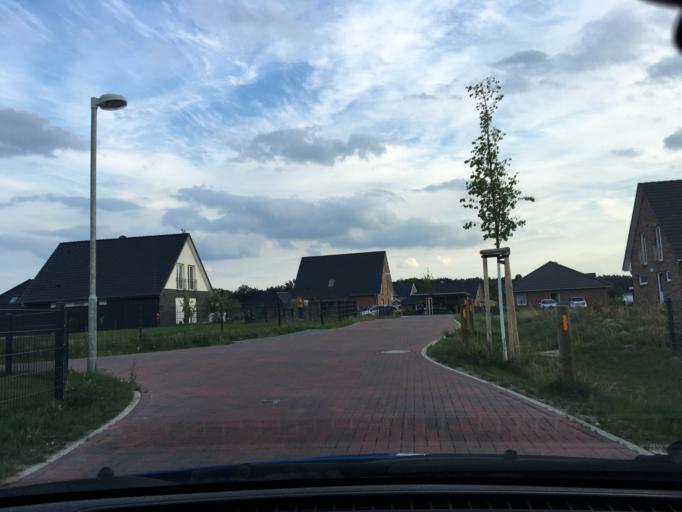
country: DE
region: Lower Saxony
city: Westergellersen
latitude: 53.2343
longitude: 10.2539
